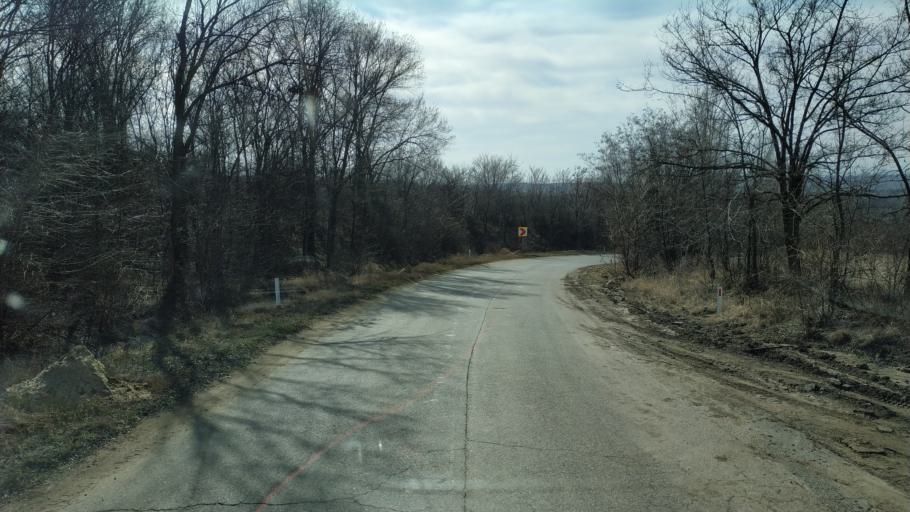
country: MD
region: Nisporeni
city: Nisporeni
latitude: 46.9555
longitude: 28.2328
